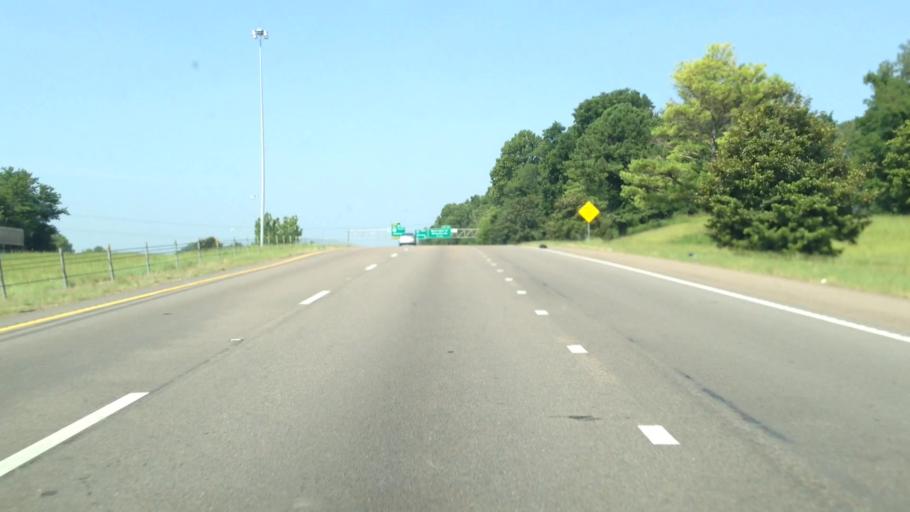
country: US
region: Mississippi
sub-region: Warren County
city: Vicksburg
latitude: 32.3167
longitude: -90.8825
